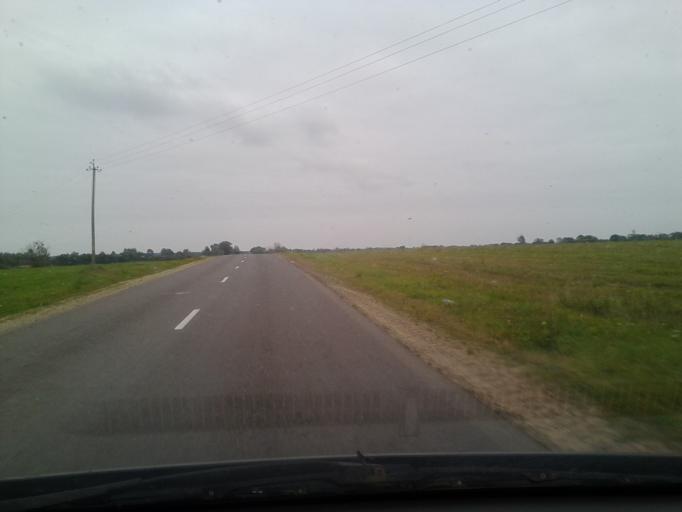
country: BY
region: Vitebsk
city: Pastavy
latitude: 55.1348
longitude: 26.9430
